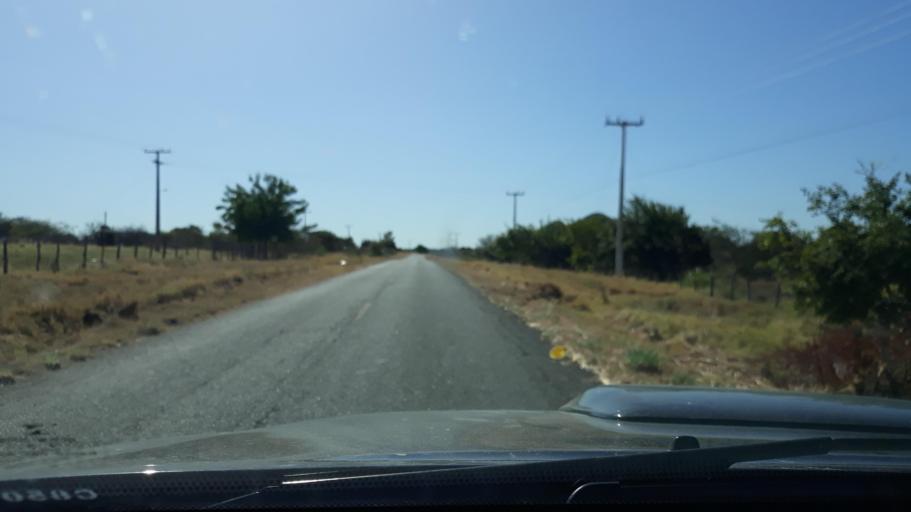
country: BR
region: Bahia
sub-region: Guanambi
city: Guanambi
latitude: -14.0877
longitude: -42.8745
